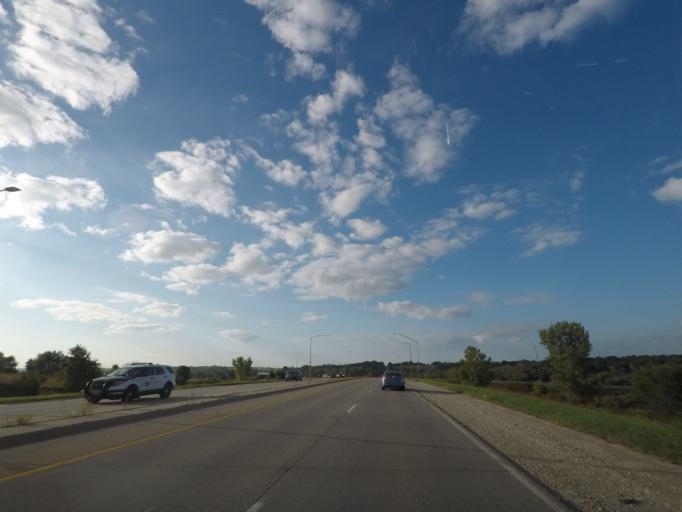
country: US
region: Iowa
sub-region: Warren County
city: Norwalk
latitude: 41.5106
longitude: -93.6451
